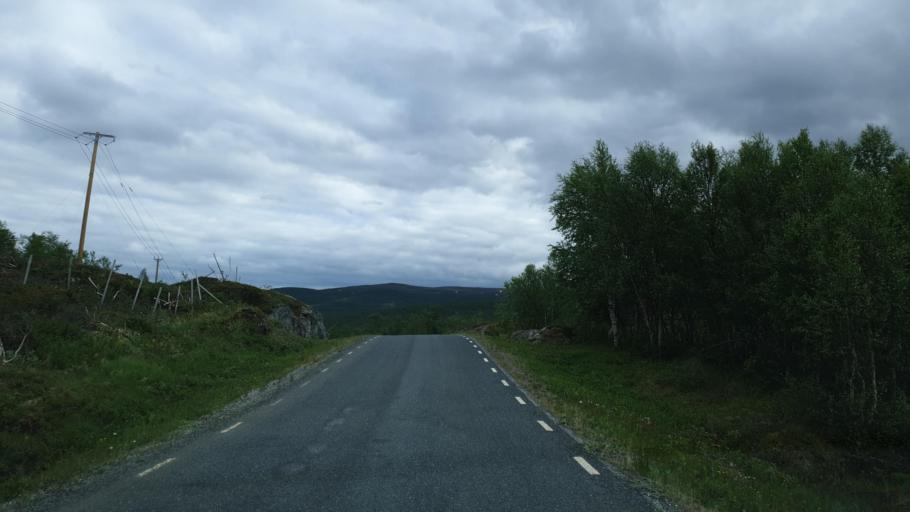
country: NO
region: Nordland
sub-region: Hattfjelldal
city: Hattfjelldal
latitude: 65.4173
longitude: 14.6853
